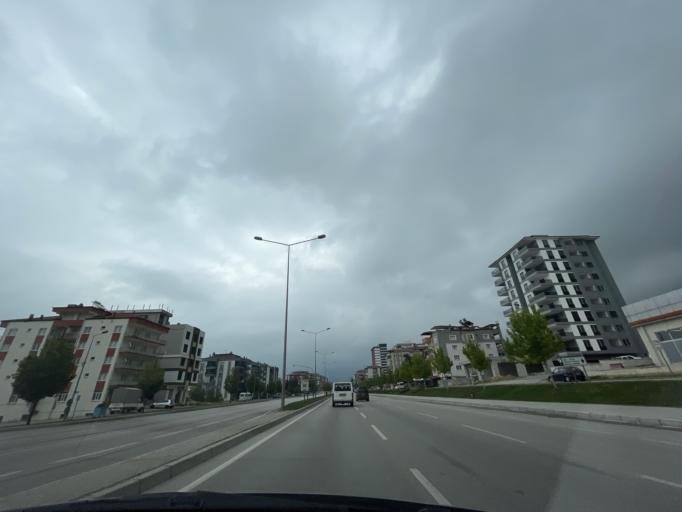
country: TR
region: Denizli
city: Denizli
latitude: 37.7325
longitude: 29.1297
